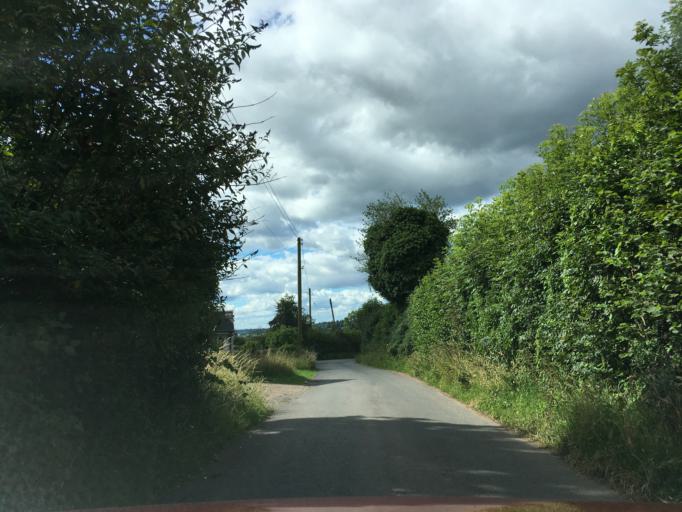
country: GB
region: England
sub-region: Gloucestershire
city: Cinderford
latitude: 51.8291
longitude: -2.4523
